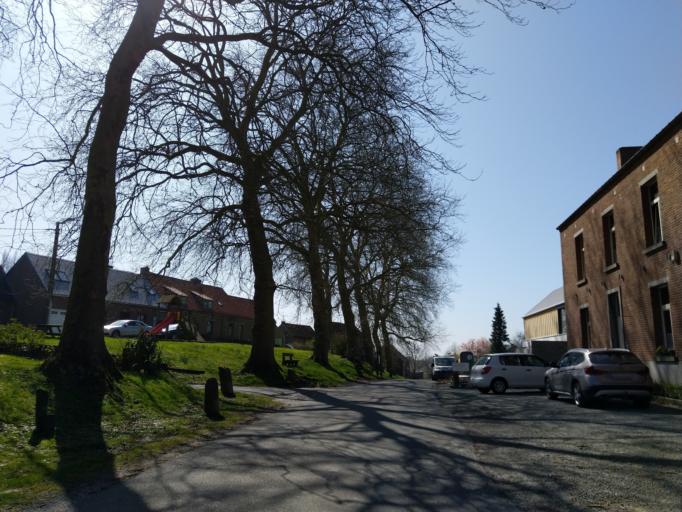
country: BE
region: Wallonia
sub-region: Province du Hainaut
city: Silly
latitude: 50.6144
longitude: 3.9527
